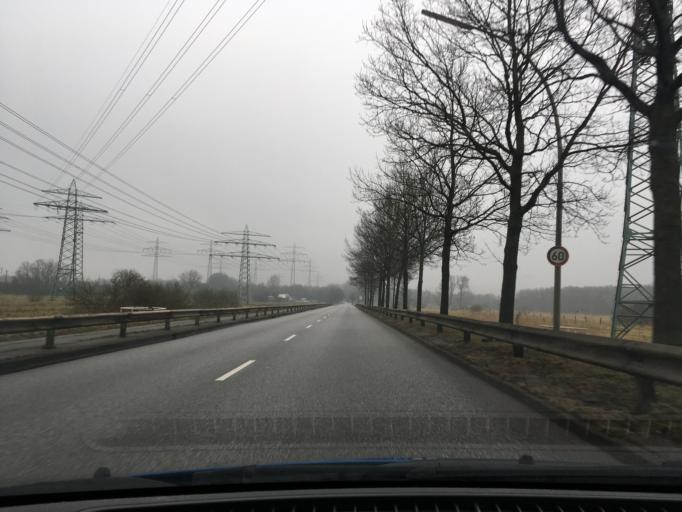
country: DE
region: Hamburg
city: Altona
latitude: 53.4896
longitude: 9.9068
